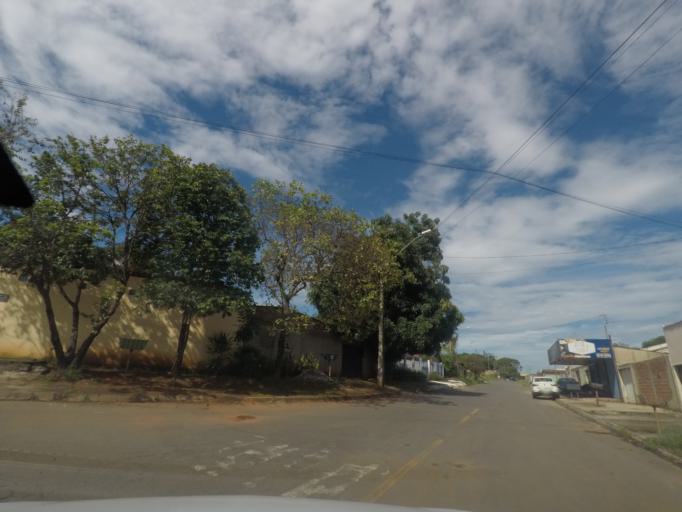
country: BR
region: Goias
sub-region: Aparecida De Goiania
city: Aparecida de Goiania
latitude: -16.7975
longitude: -49.2649
